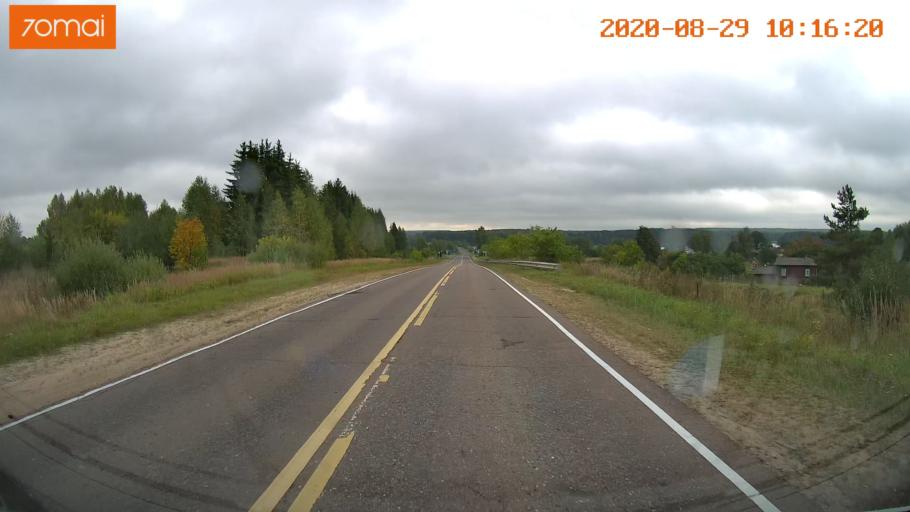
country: RU
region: Ivanovo
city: Yur'yevets
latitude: 57.3386
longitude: 42.7905
